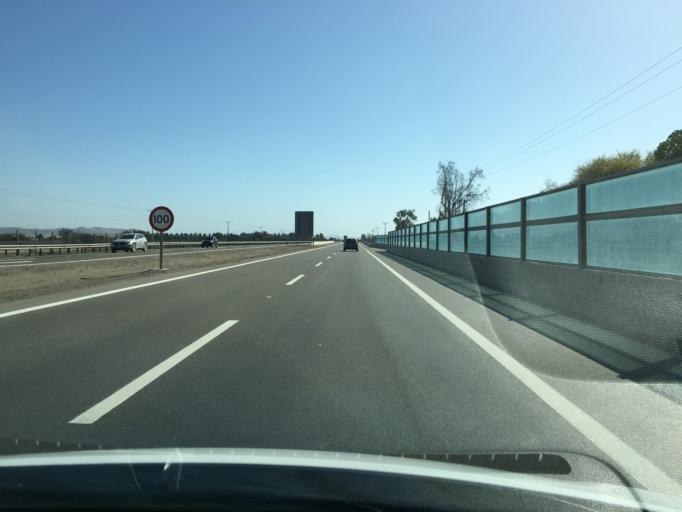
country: CL
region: Atacama
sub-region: Provincia de Copiapo
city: Copiapo
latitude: -27.3230
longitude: -70.5423
